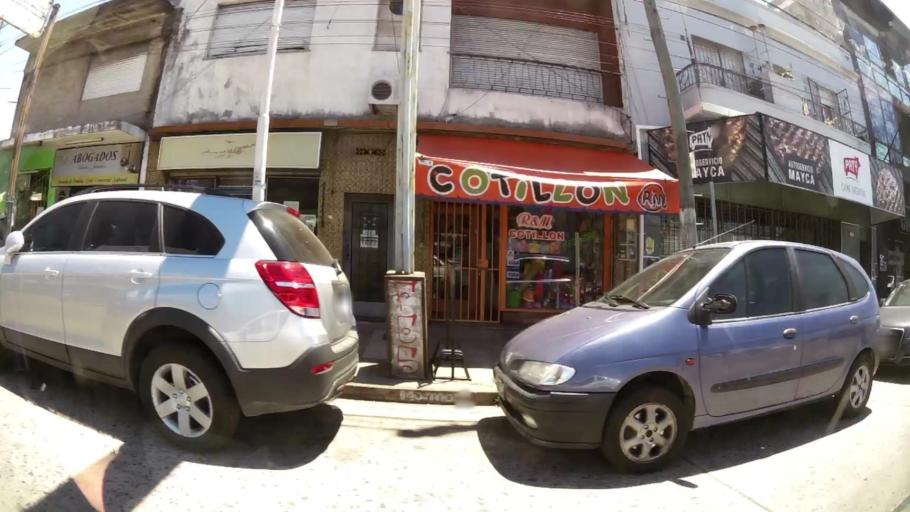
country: AR
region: Buenos Aires
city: Caseros
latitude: -34.5930
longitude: -58.5613
